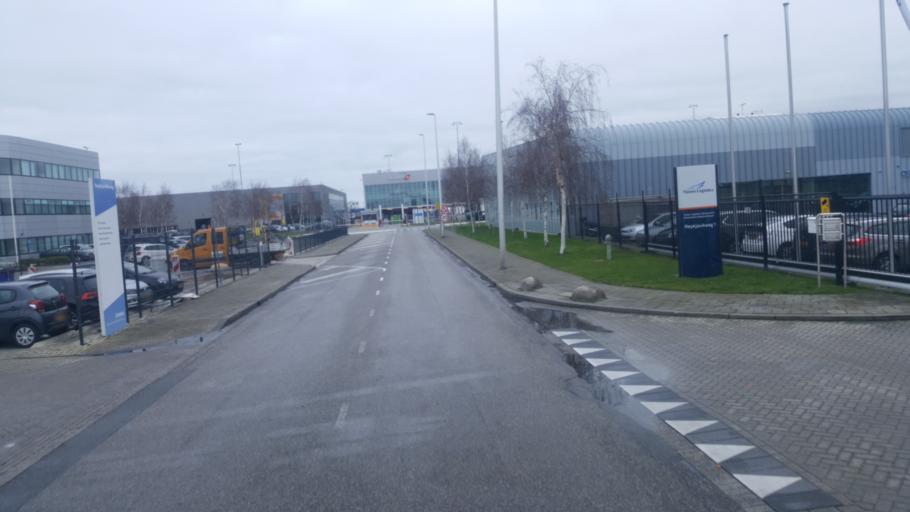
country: NL
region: North Holland
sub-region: Gemeente Aalsmeer
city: Aalsmeer
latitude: 52.2940
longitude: 4.7708
